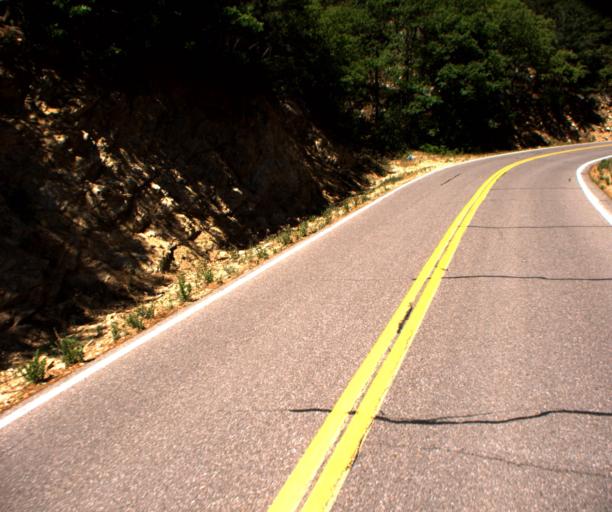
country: US
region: Arizona
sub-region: Graham County
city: Swift Trail Junction
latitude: 32.6360
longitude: -109.8454
